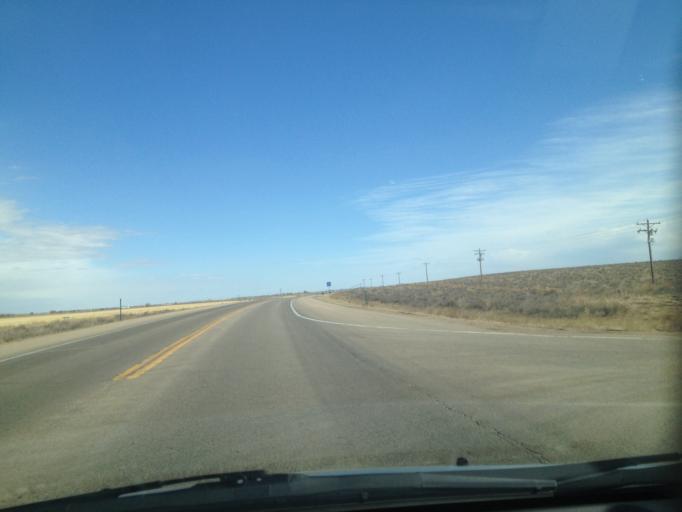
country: US
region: Colorado
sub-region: Weld County
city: Kersey
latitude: 40.2936
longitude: -104.2918
